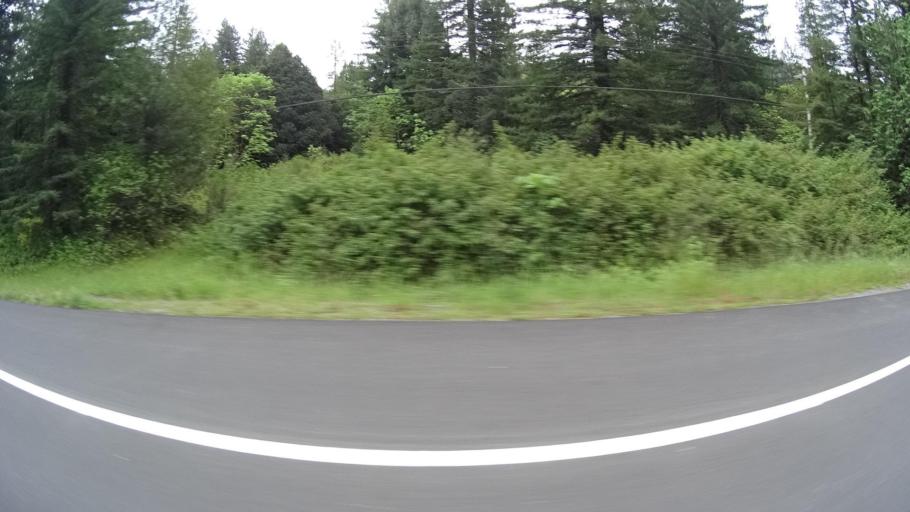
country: US
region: California
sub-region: Humboldt County
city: Rio Dell
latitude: 40.4400
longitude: -124.0273
